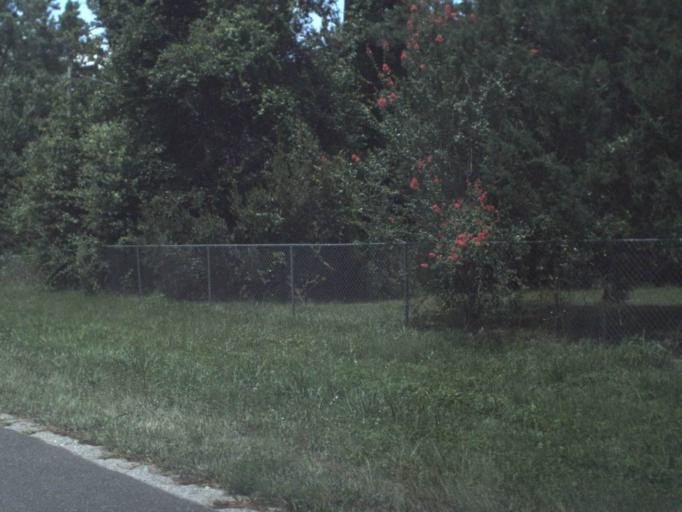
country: US
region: Florida
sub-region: Clay County
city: Keystone Heights
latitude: 29.8387
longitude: -82.0648
